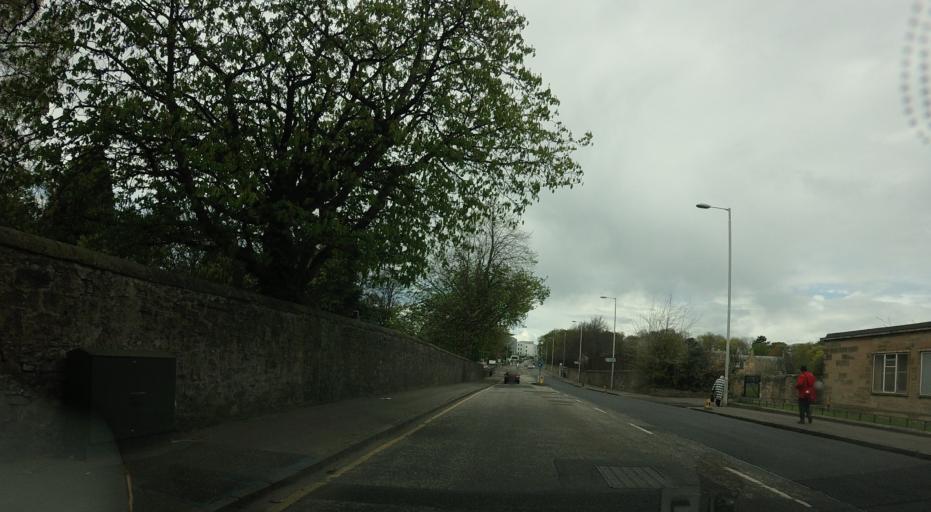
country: GB
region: Scotland
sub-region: Edinburgh
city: Edinburgh
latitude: 55.9594
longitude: -3.2275
